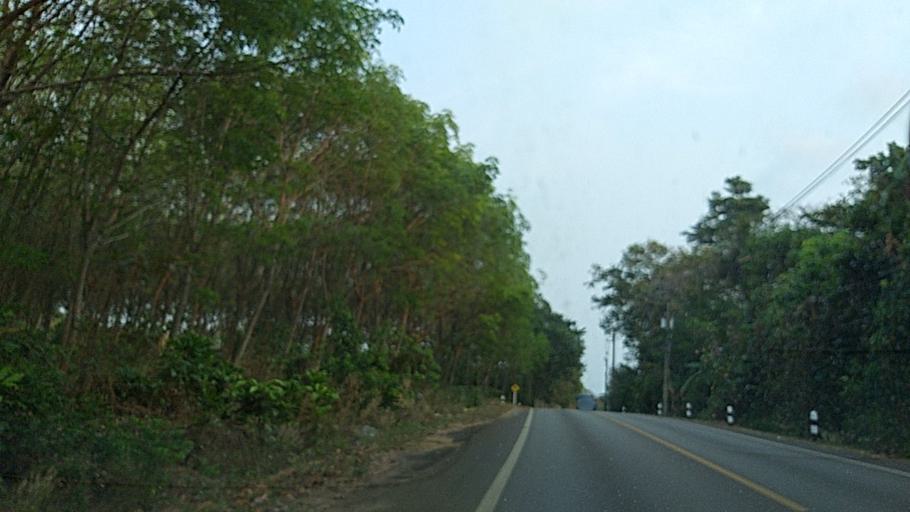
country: TH
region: Trat
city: Laem Ngop
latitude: 12.1947
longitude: 102.2893
